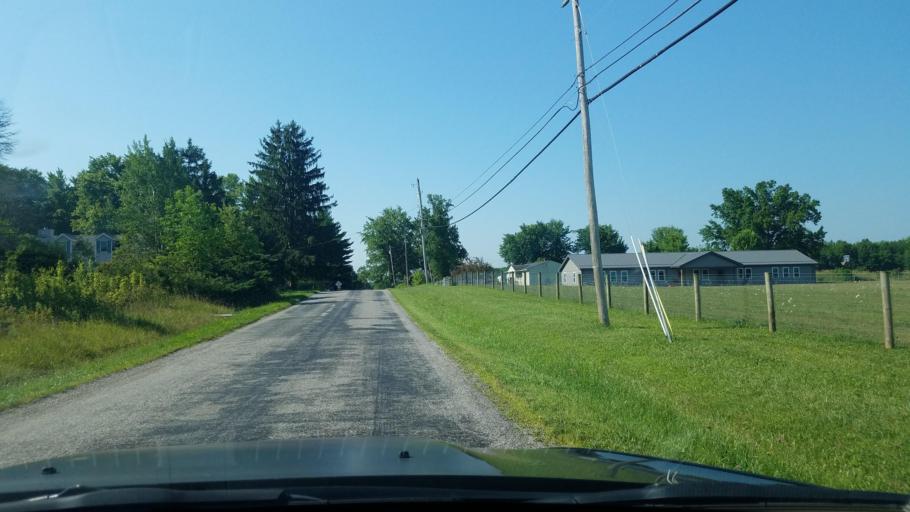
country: US
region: Ohio
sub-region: Trumbull County
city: Leavittsburg
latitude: 41.2793
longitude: -80.9254
